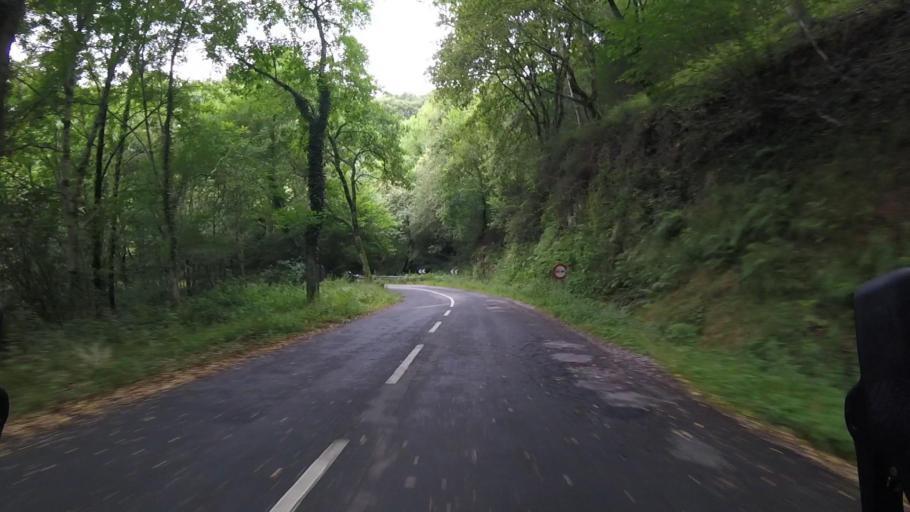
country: ES
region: Basque Country
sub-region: Provincia de Guipuzcoa
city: Irun
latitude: 43.2717
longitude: -1.8093
